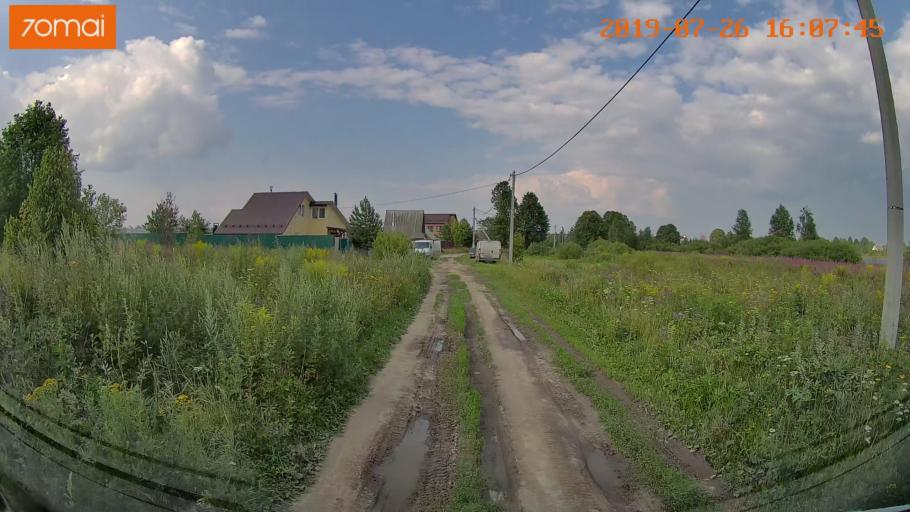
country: RU
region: Ivanovo
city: Bogorodskoye
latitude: 57.0610
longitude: 41.0570
